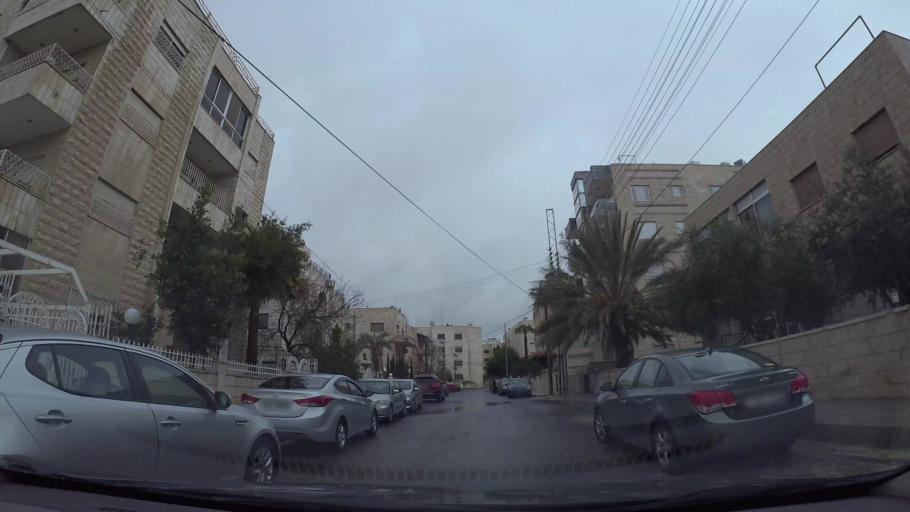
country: JO
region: Amman
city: Wadi as Sir
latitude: 31.9617
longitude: 35.8639
